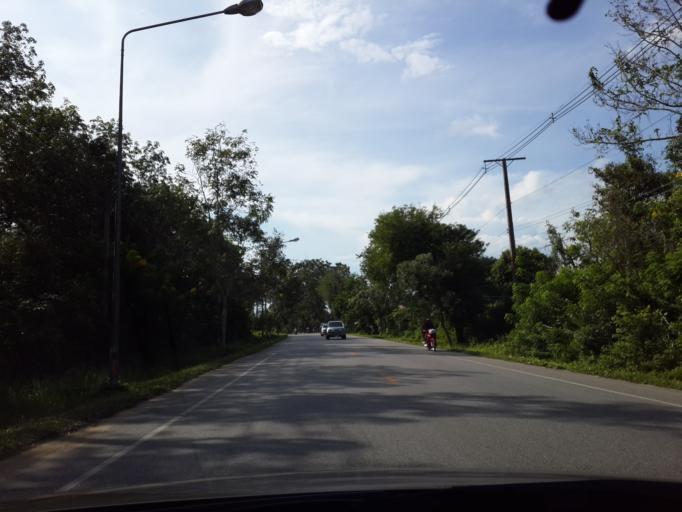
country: TH
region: Yala
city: Yala
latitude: 6.4963
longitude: 101.2987
